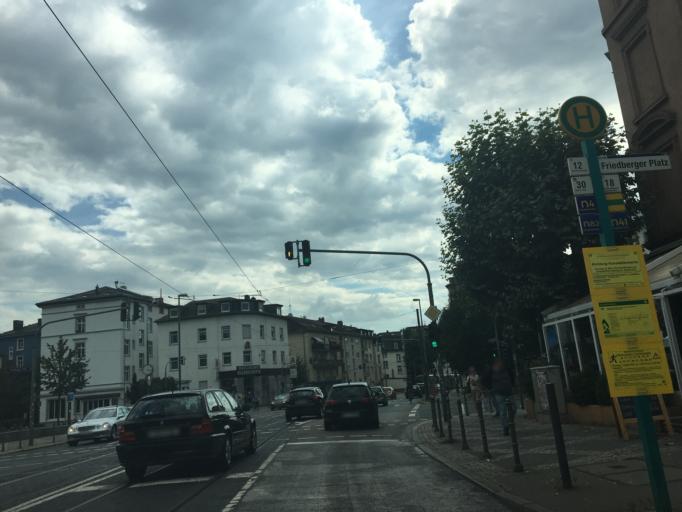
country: DE
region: Hesse
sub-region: Regierungsbezirk Darmstadt
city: Frankfurt am Main
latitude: 50.1237
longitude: 8.6917
